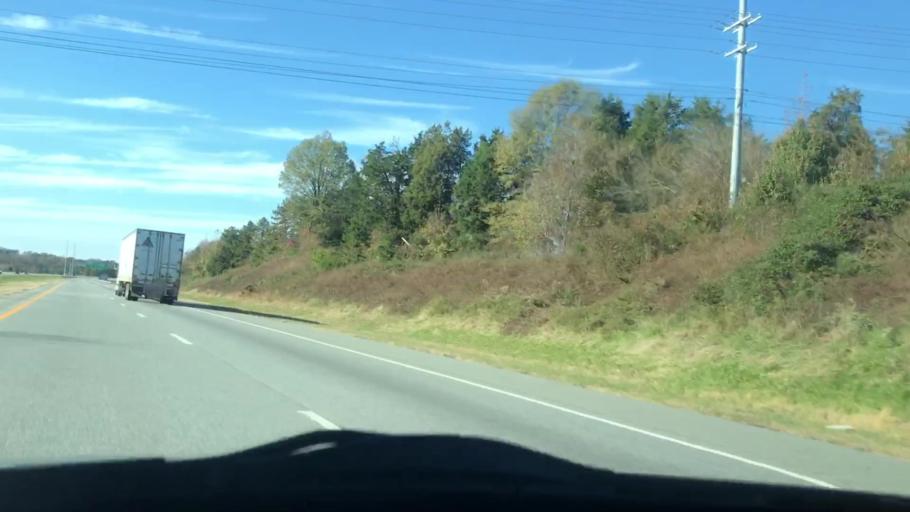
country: US
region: North Carolina
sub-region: Randolph County
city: Archdale
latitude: 35.9400
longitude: -79.9632
